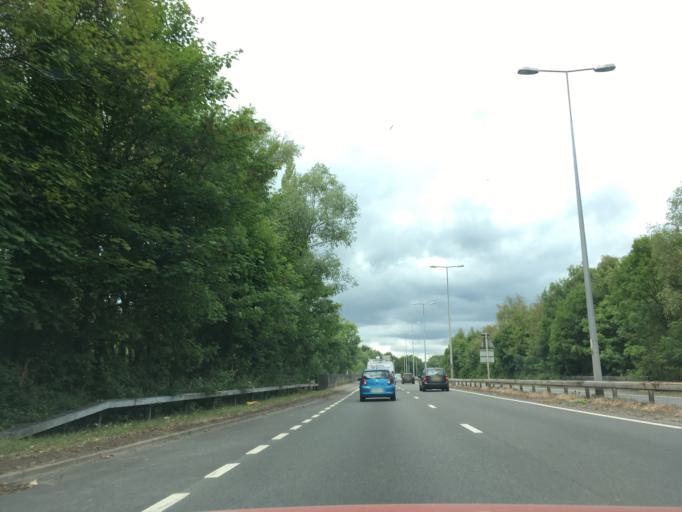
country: GB
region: Wales
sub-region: Torfaen County Borough
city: New Inn
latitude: 51.6842
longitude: -3.0187
